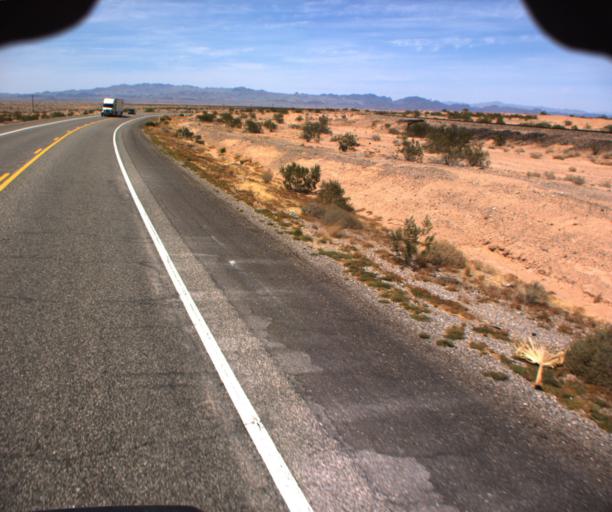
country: US
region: Arizona
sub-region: La Paz County
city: Parker
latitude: 34.0299
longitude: -114.2571
